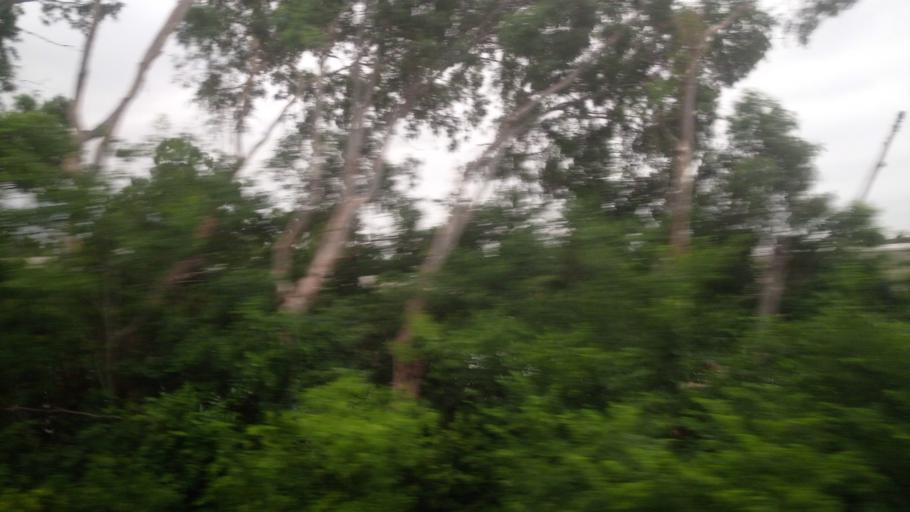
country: AU
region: New South Wales
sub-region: Penrith Municipality
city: Penrith
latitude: -33.7480
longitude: 150.6865
